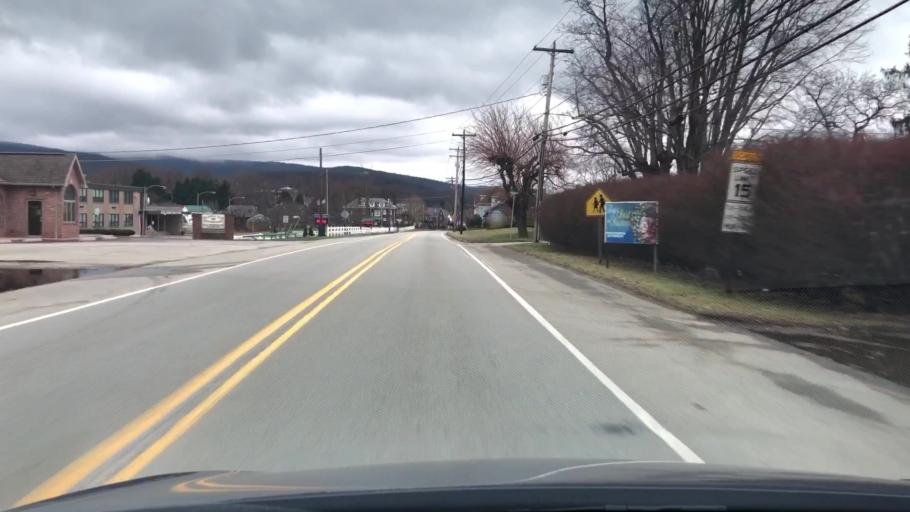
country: US
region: Pennsylvania
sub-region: Fayette County
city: Connellsville
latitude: 40.0277
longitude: -79.5810
